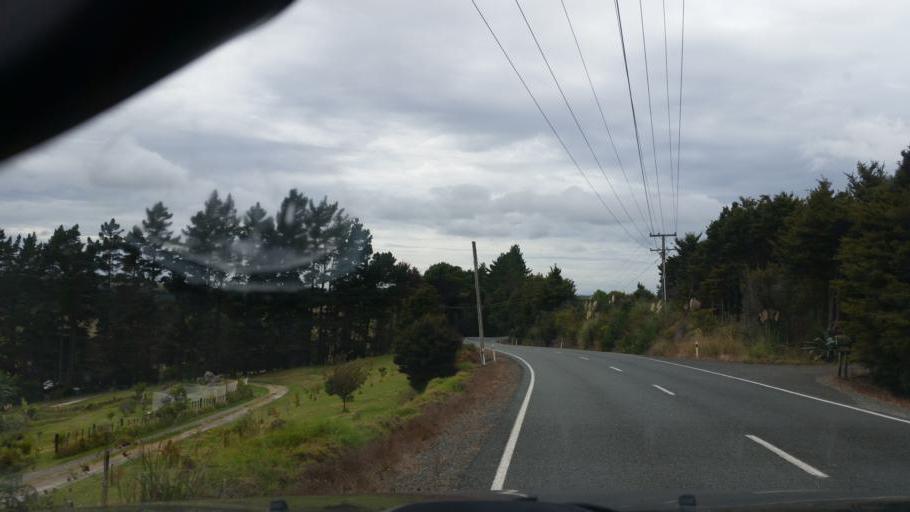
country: NZ
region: Auckland
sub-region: Auckland
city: Wellsford
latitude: -36.1323
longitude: 174.5430
